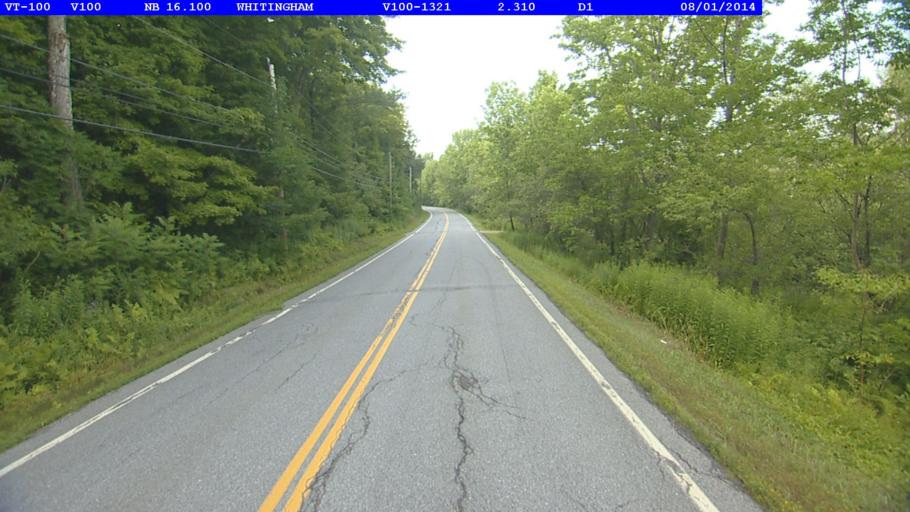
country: US
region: Massachusetts
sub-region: Franklin County
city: Charlemont
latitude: 42.7717
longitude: -72.8940
